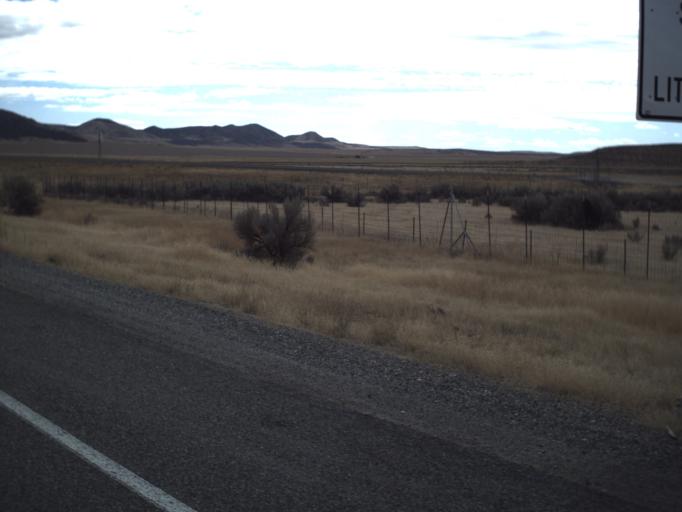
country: US
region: Idaho
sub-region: Oneida County
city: Malad City
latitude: 41.9651
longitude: -112.7608
